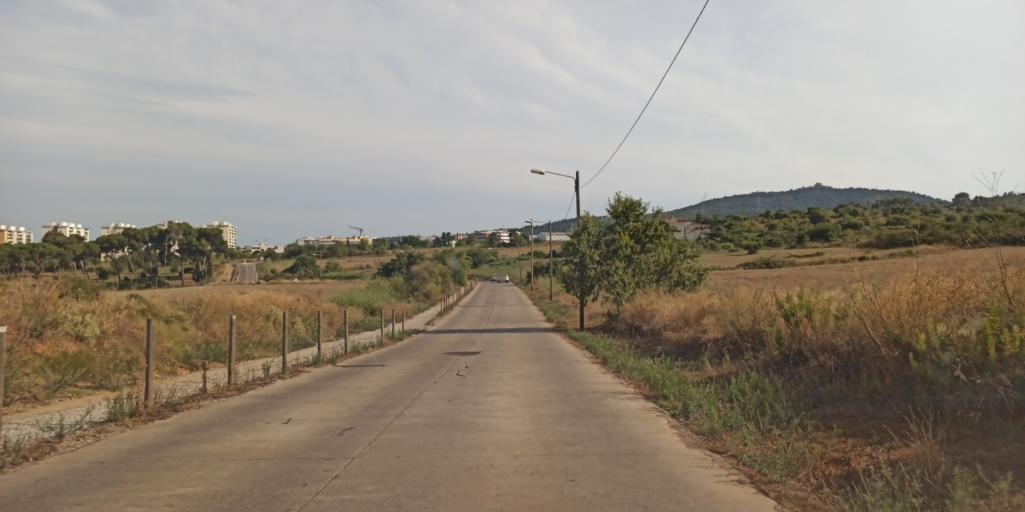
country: ES
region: Catalonia
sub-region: Provincia de Barcelona
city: Santa Coloma de Cervello
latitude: 41.3627
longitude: 2.0238
